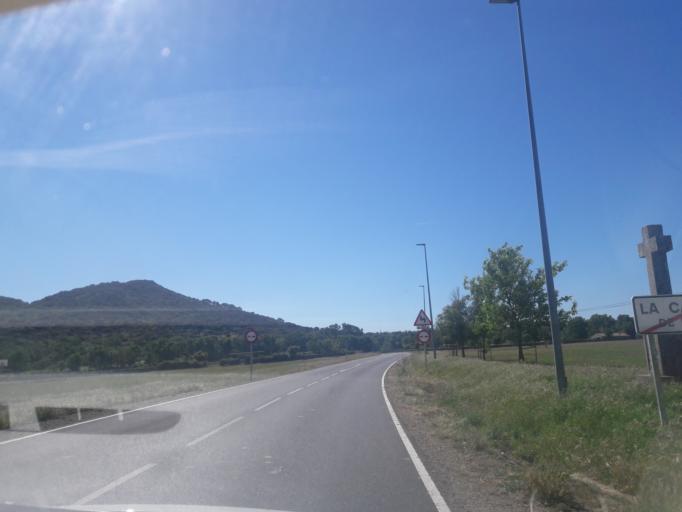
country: ES
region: Castille and Leon
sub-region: Provincia de Salamanca
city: Nava de Bejar
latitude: 40.4943
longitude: -5.6630
